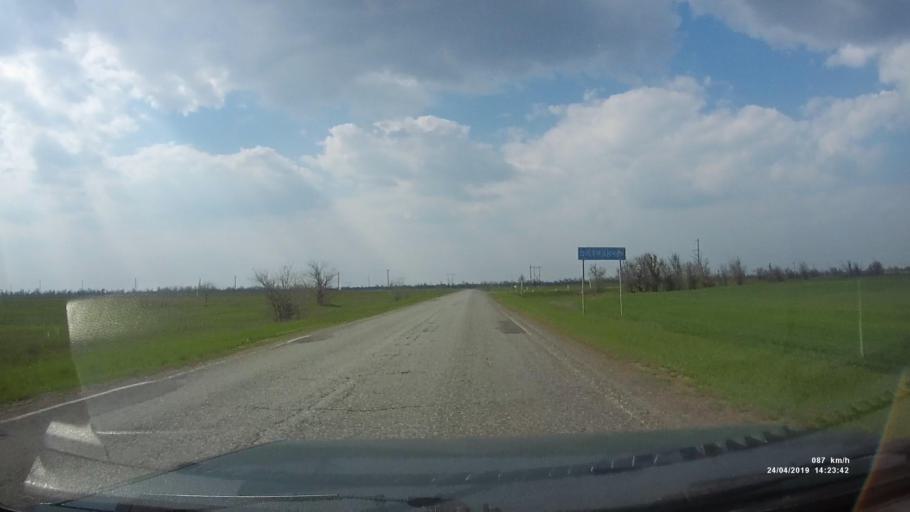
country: RU
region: Kalmykiya
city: Arshan'
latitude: 46.3244
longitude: 44.1104
